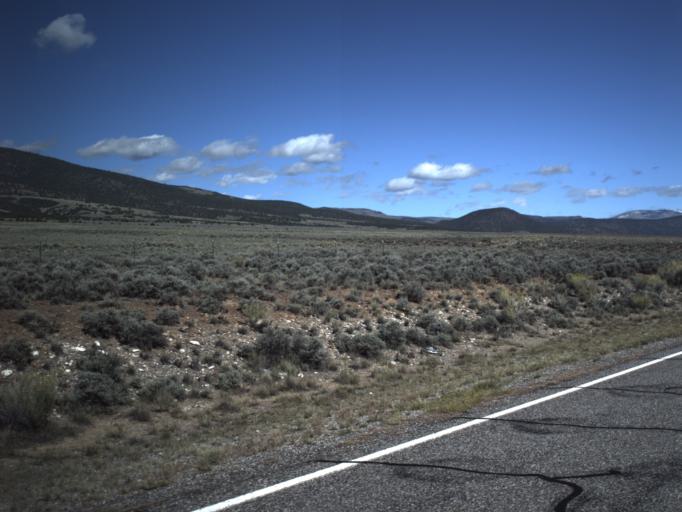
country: US
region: Utah
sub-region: Wayne County
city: Loa
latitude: 38.3677
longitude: -111.9399
